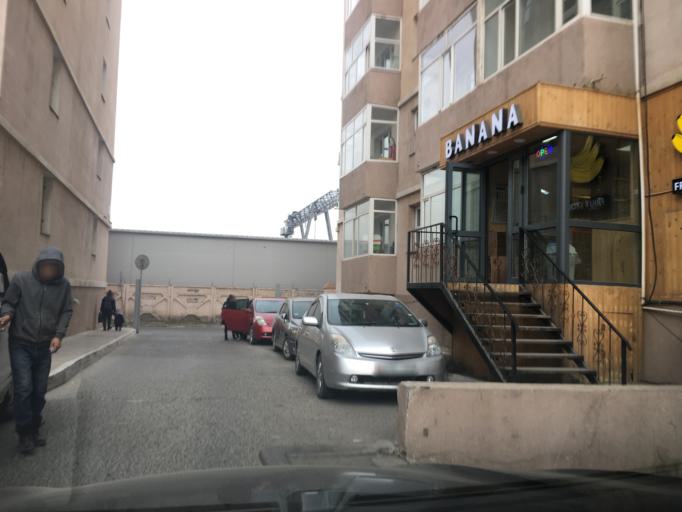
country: MN
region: Ulaanbaatar
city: Ulaanbaatar
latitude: 47.9032
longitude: 106.8904
